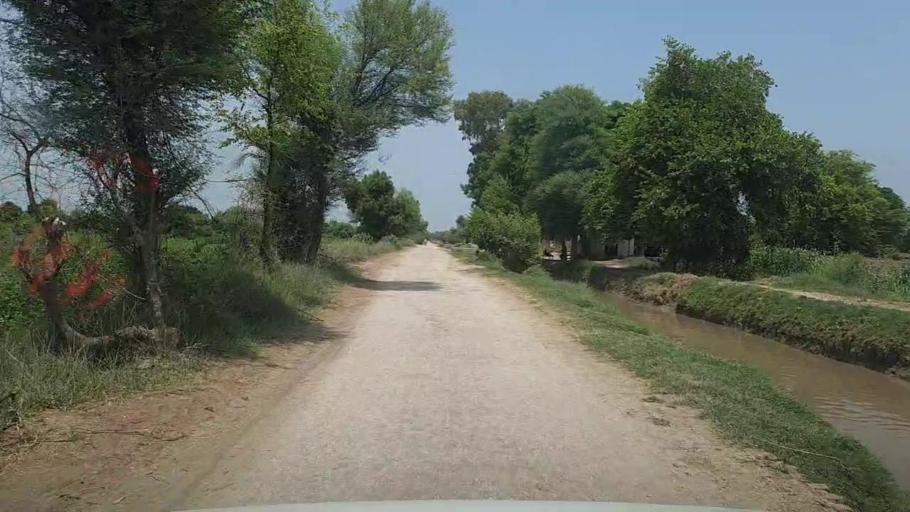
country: PK
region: Sindh
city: Karaundi
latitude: 26.8954
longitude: 68.3321
